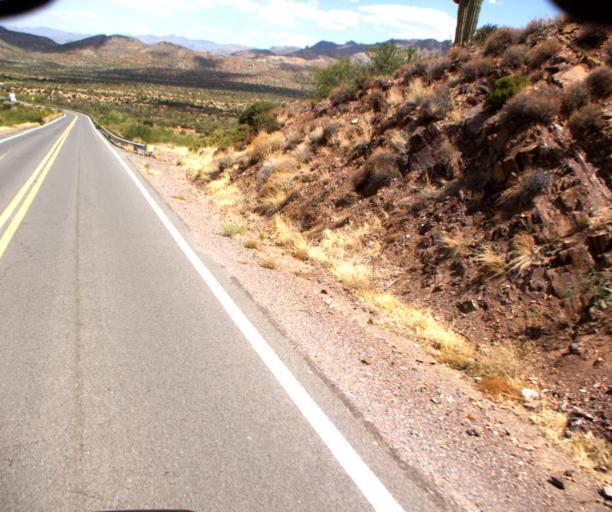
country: US
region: Arizona
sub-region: Pinal County
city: Superior
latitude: 33.2110
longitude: -111.0610
